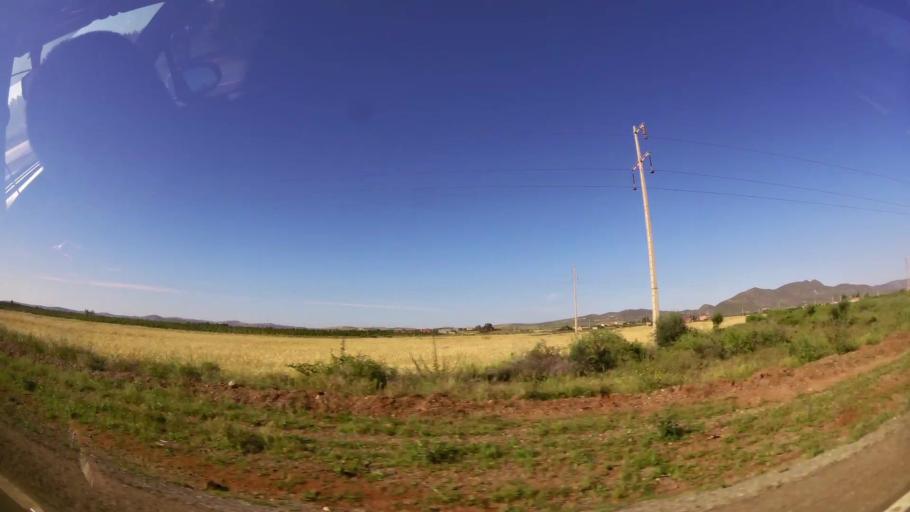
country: MA
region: Oriental
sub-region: Berkane-Taourirt
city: Ahfir
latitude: 34.9919
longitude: -2.1590
